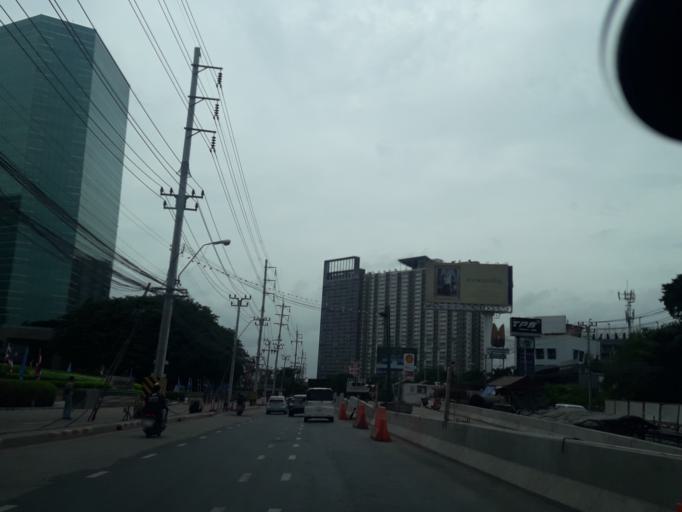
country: TH
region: Bangkok
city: Chatuchak
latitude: 13.8281
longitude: 100.5656
